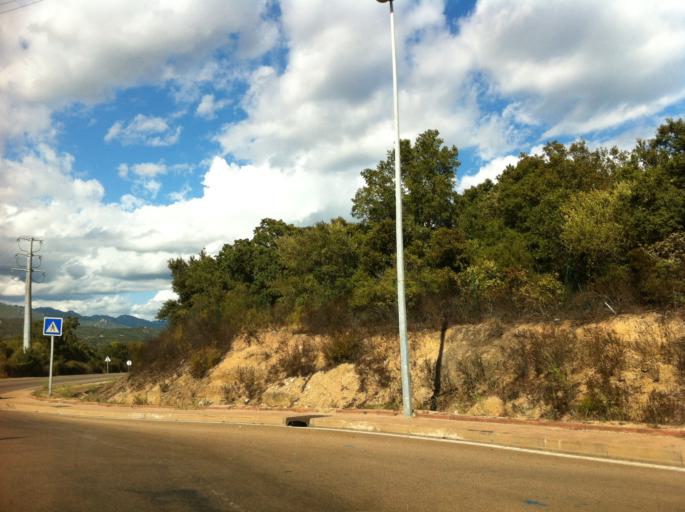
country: FR
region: Corsica
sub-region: Departement de la Corse-du-Sud
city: Porto-Vecchio
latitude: 41.5924
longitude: 9.2645
